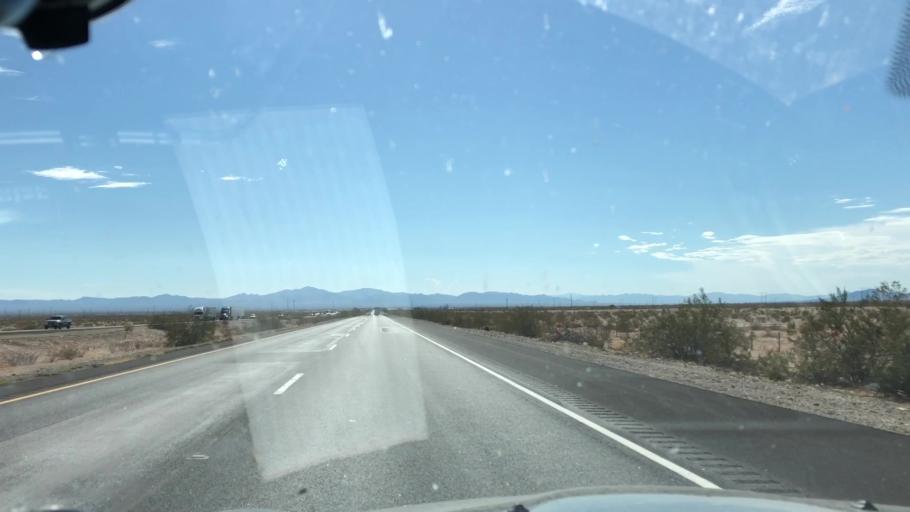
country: US
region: California
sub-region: Riverside County
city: Mesa Verde
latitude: 33.6092
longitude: -114.8696
